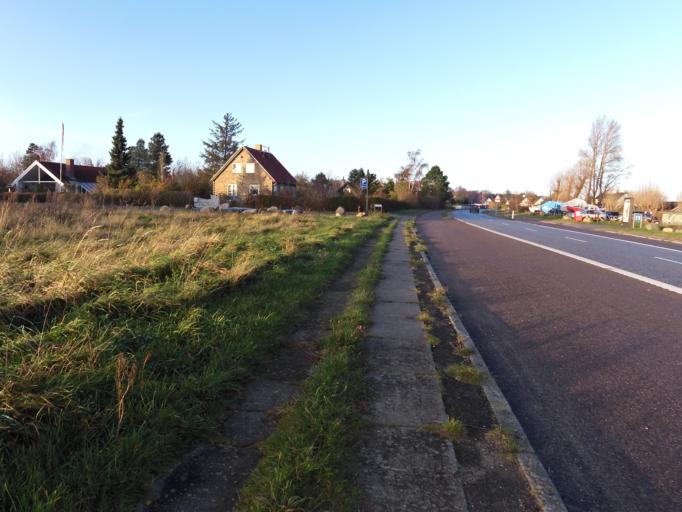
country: DK
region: Central Jutland
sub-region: Arhus Kommune
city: Beder
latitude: 56.0230
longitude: 10.2607
